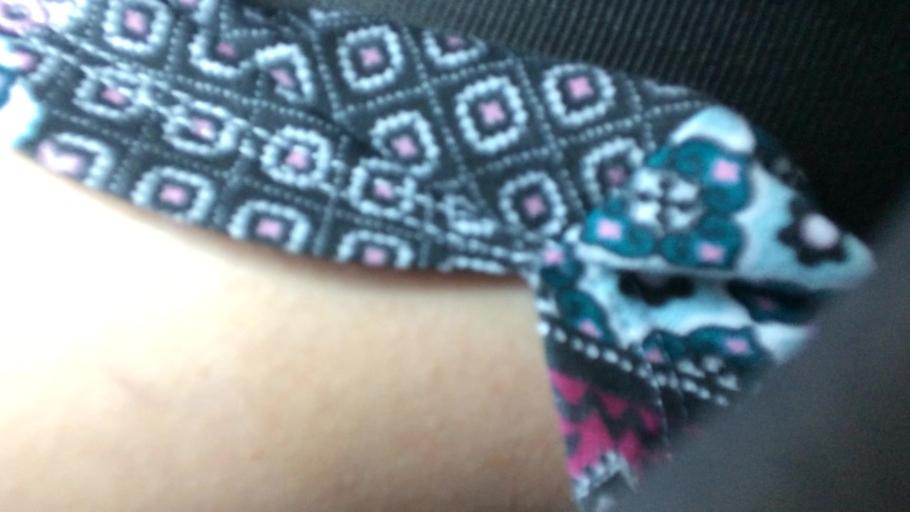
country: US
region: New Mexico
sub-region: Colfax County
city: Springer
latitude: 36.2075
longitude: -104.6624
